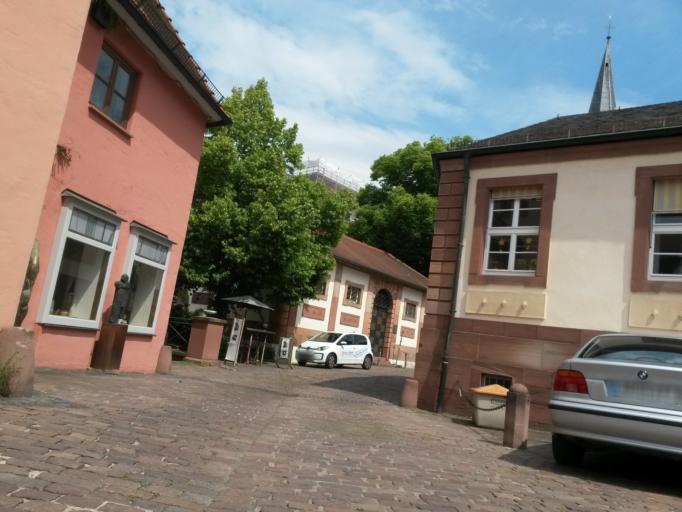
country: DE
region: Bavaria
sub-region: Regierungsbezirk Unterfranken
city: Aschaffenburg
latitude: 49.9729
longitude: 9.1452
